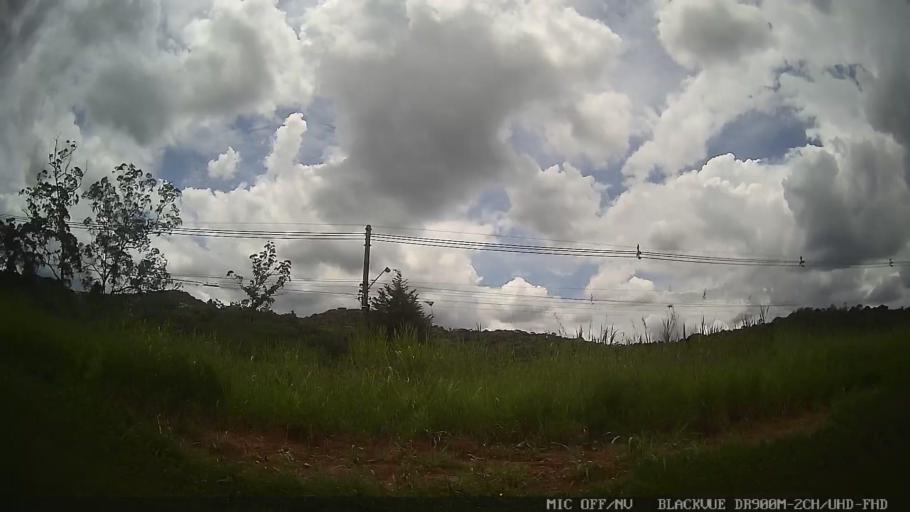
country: BR
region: Sao Paulo
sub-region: Suzano
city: Suzano
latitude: -23.6224
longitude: -46.3224
